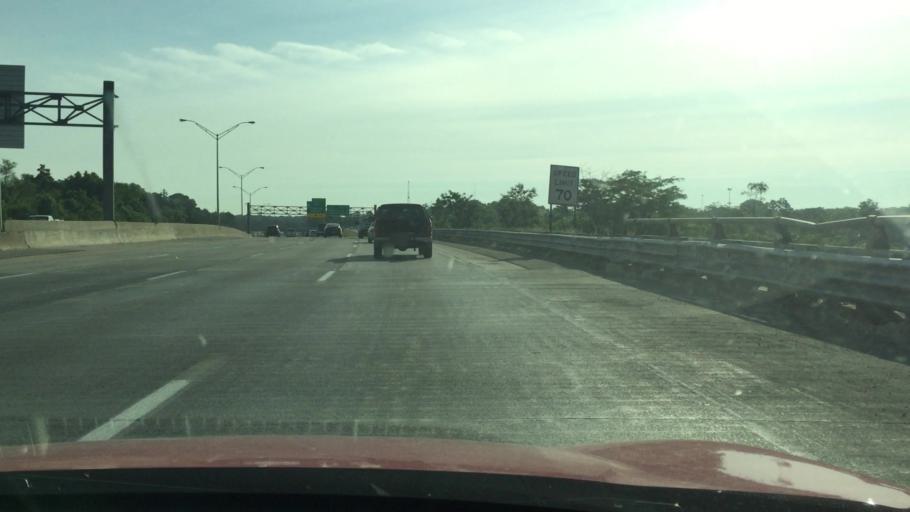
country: US
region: Michigan
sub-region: Genesee County
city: Flint
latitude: 43.0046
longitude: -83.6937
